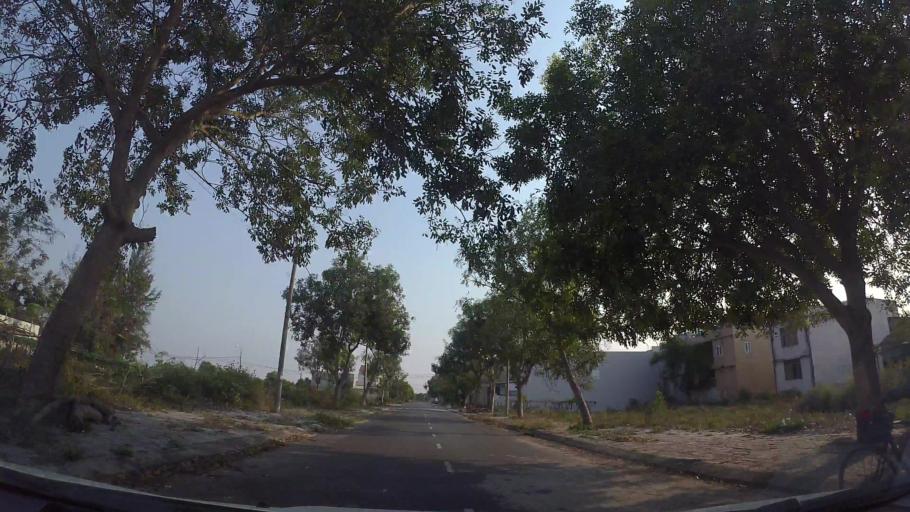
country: VN
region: Da Nang
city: Ngu Hanh Son
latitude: 15.9683
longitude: 108.2555
